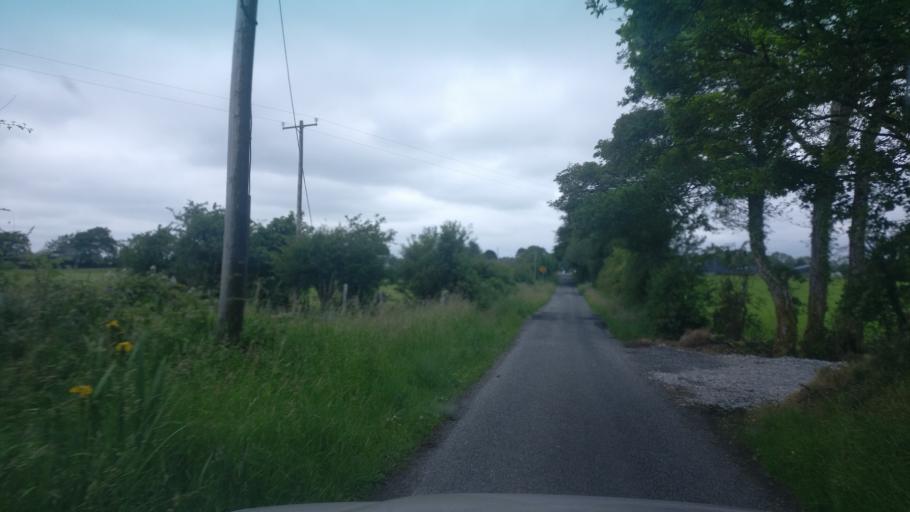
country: IE
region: Connaught
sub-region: County Galway
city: Ballinasloe
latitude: 53.3033
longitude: -8.3614
